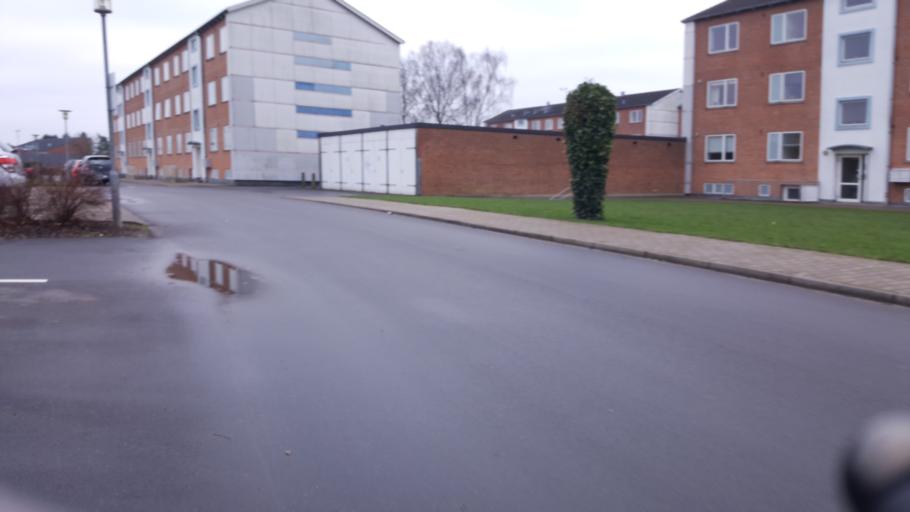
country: DK
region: South Denmark
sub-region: Kolding Kommune
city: Kolding
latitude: 55.4771
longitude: 9.4820
